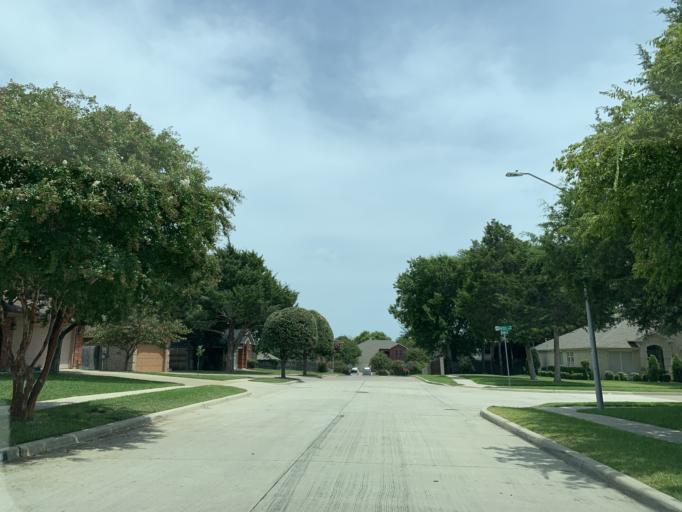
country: US
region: Texas
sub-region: Dallas County
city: Grand Prairie
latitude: 32.6627
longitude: -97.0247
